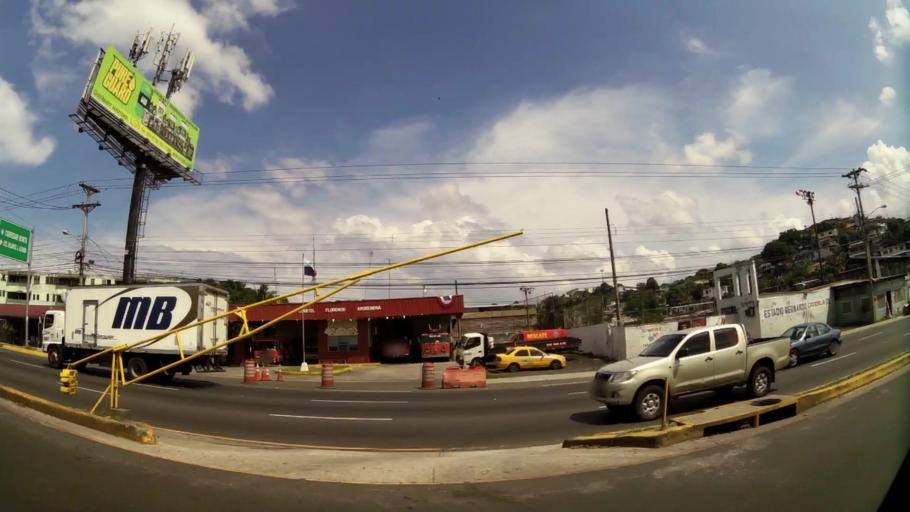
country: PA
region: Panama
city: San Miguelito
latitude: 9.0302
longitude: -79.4991
